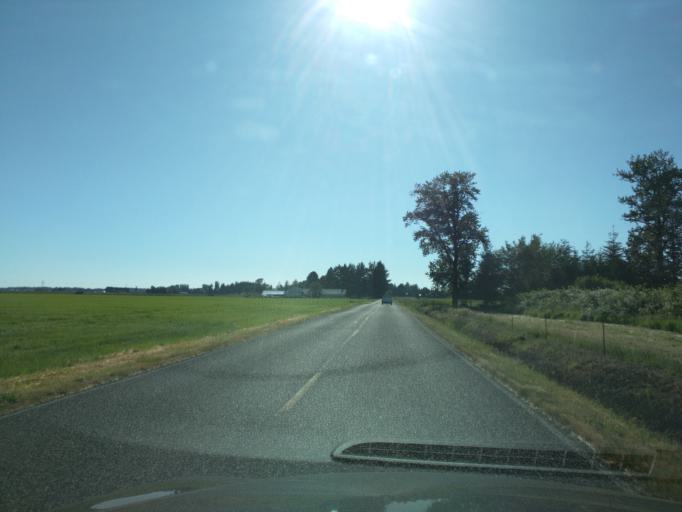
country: US
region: Washington
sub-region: Whatcom County
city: Lynden
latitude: 48.9791
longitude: -122.4449
